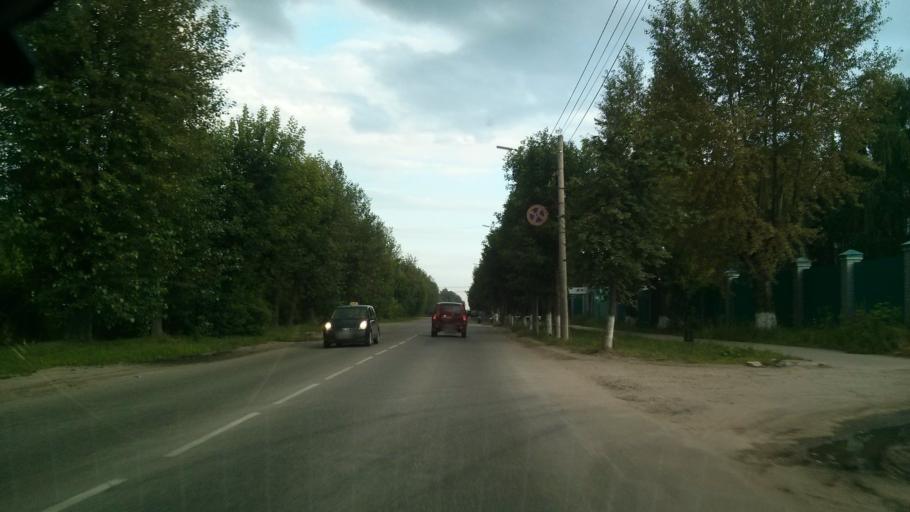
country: RU
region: Vladimir
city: Murom
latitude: 55.5560
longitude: 42.0466
